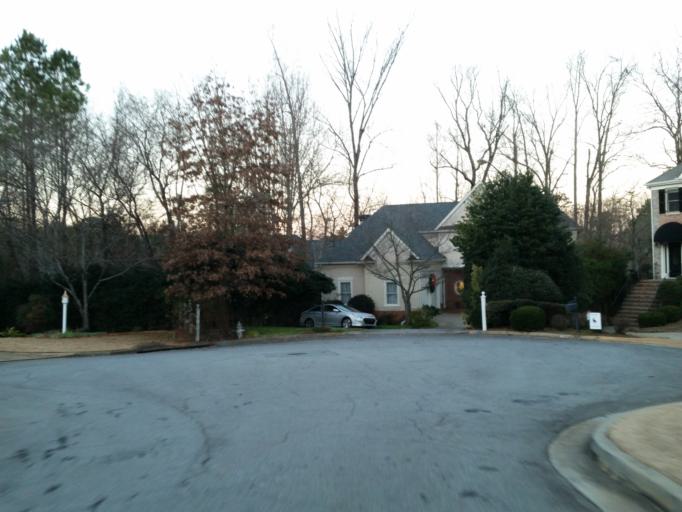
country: US
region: Georgia
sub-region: Fulton County
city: Sandy Springs
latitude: 33.9706
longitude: -84.3983
